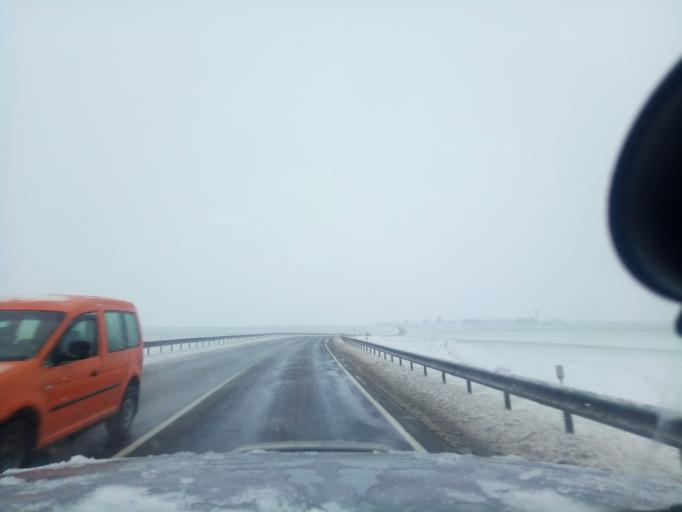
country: BY
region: Minsk
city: Haradzyeya
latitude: 53.3288
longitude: 26.5496
